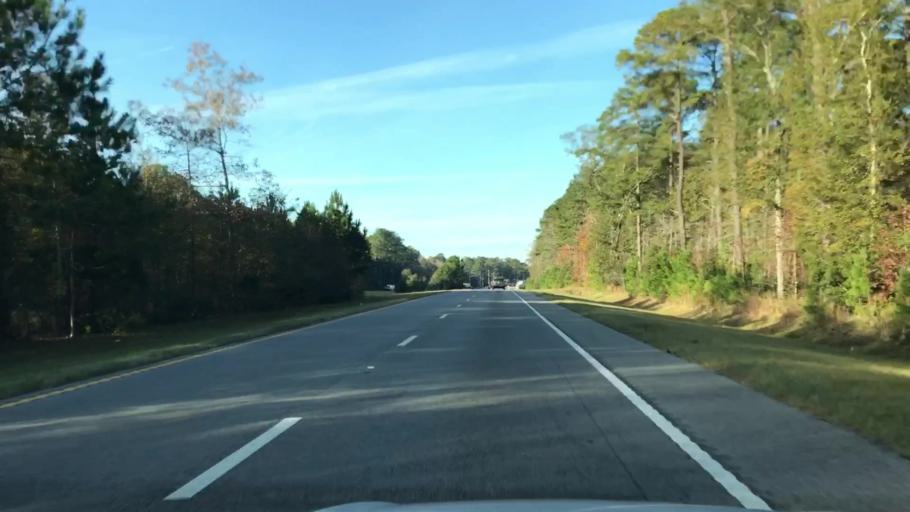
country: US
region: South Carolina
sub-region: Colleton County
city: Walterboro
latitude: 32.7375
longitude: -80.5766
